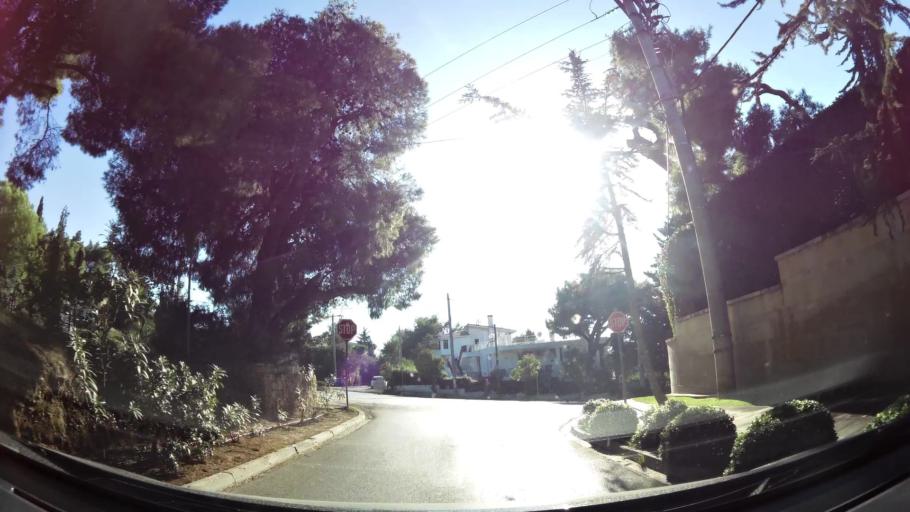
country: GR
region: Attica
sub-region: Nomarchia Athinas
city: Nea Erythraia
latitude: 38.0981
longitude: 23.8280
